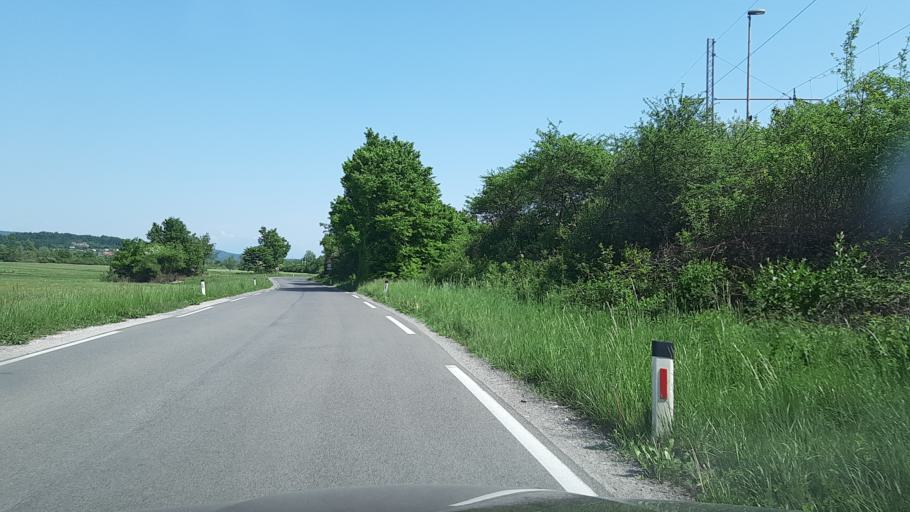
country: SI
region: Brezovica
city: Notranje Gorice
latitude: 45.9652
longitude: 14.3952
